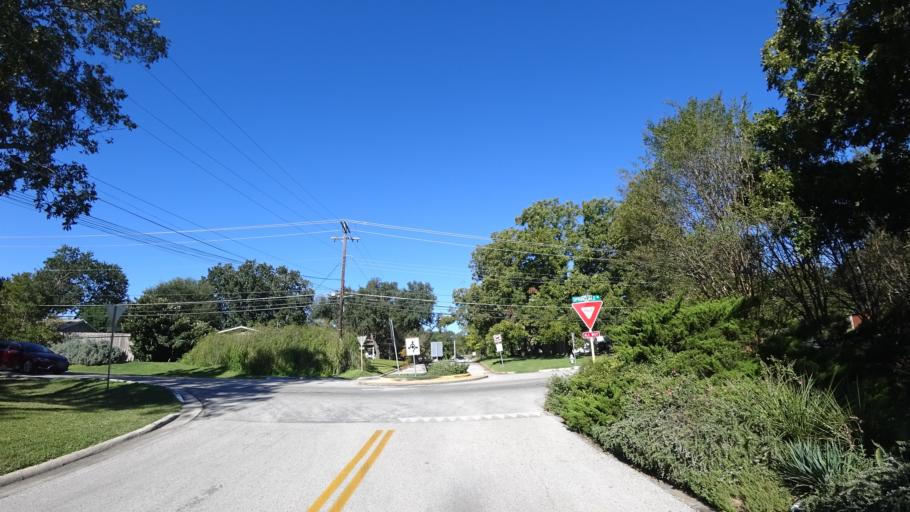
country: US
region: Texas
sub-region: Travis County
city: Manor
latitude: 30.3334
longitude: -97.6527
